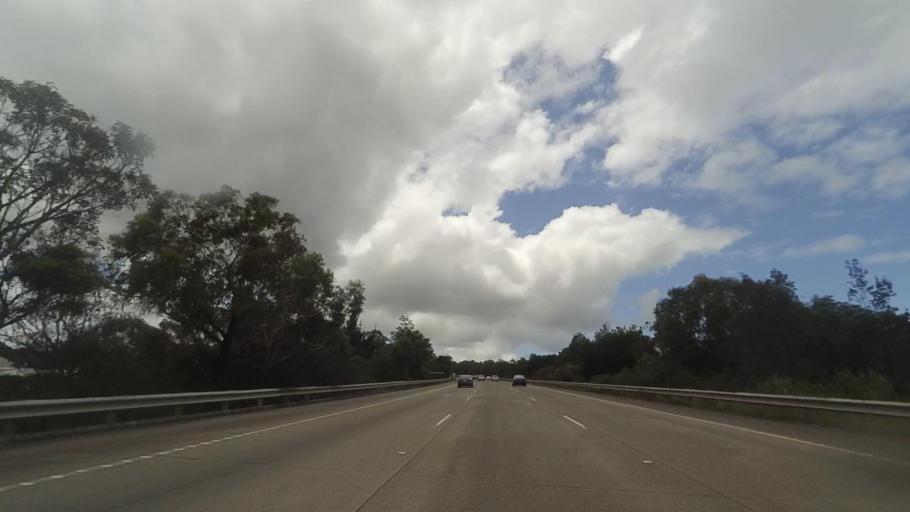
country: AU
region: New South Wales
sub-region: Gosford Shire
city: Point Clare
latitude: -33.4156
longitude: 151.2965
